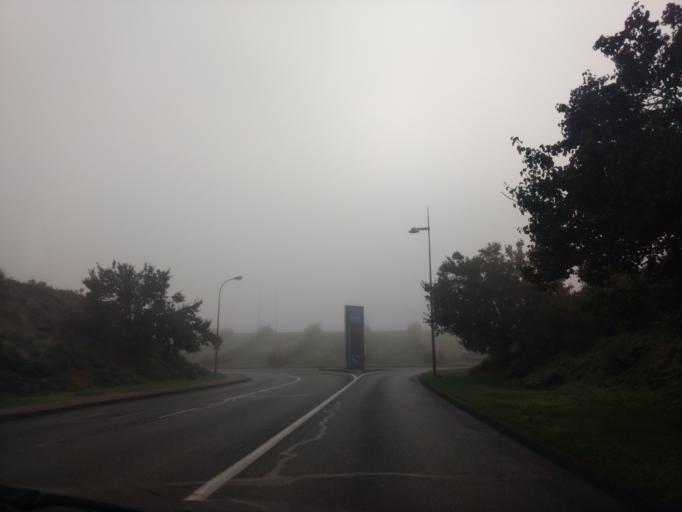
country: FR
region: Poitou-Charentes
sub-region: Departement de la Vienne
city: Chasseneuil-du-Poitou
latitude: 46.6606
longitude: 0.3675
